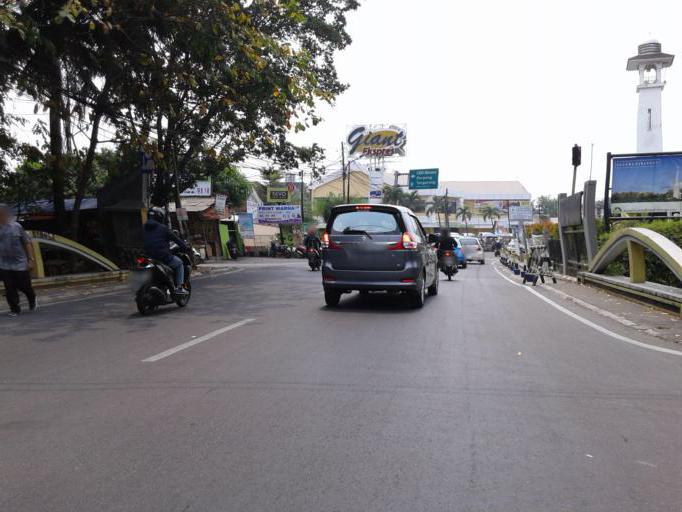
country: ID
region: Banten
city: South Tangerang
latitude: -6.2724
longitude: 106.7515
